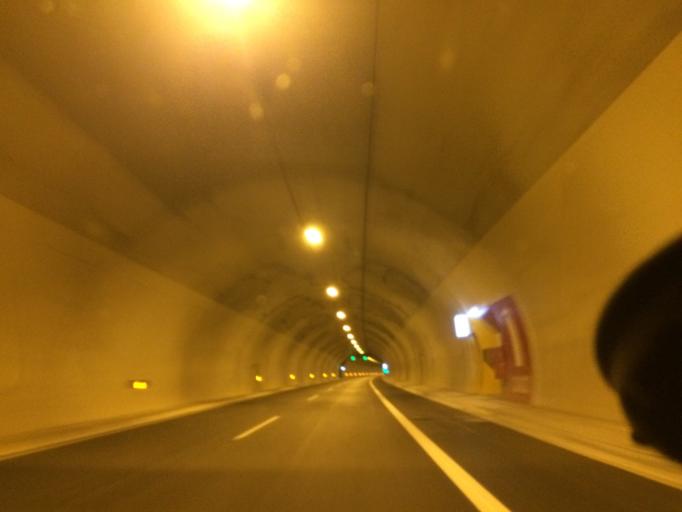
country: GR
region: Thessaly
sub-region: Nomos Larisis
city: Pyrgetos
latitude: 39.8896
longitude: 22.6101
